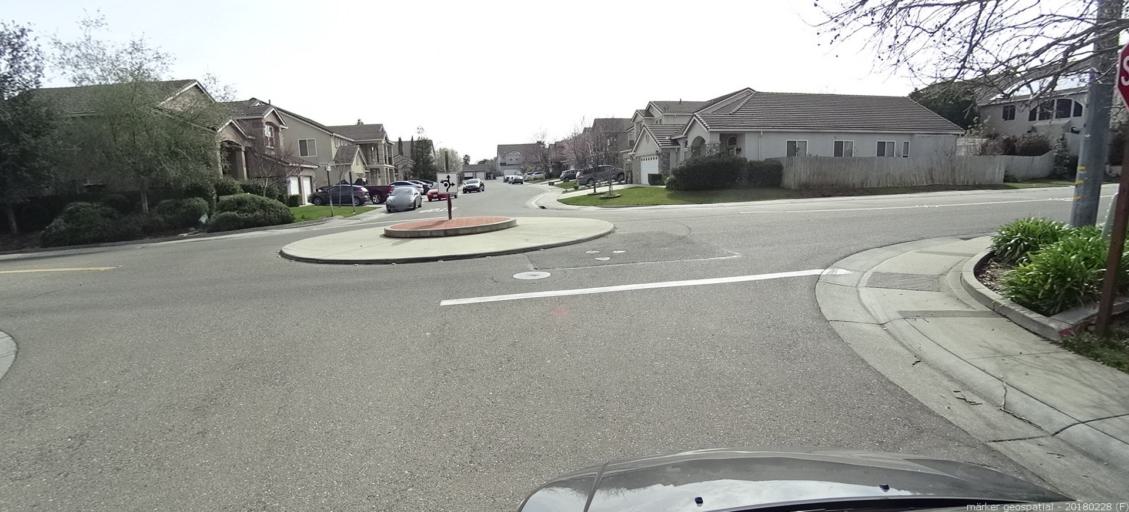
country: US
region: California
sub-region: Sacramento County
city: Antelope
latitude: 38.7108
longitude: -121.3444
